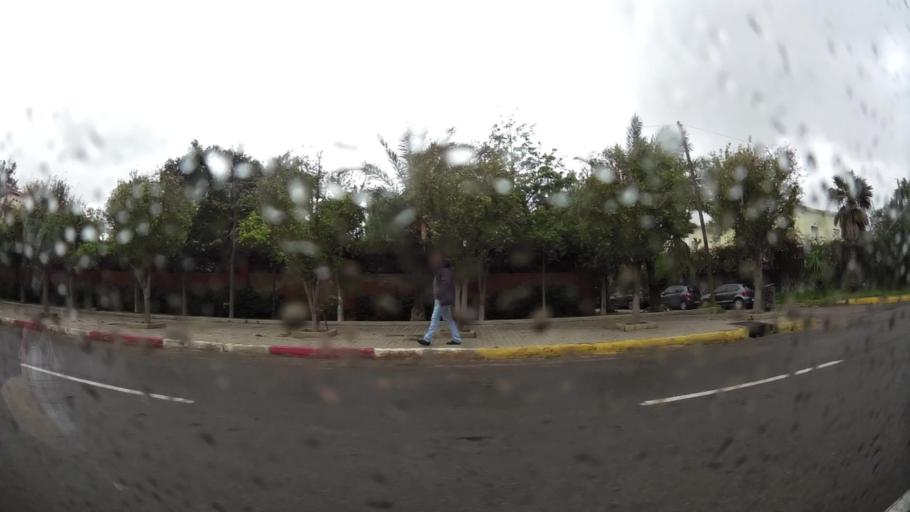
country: MA
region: Grand Casablanca
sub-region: Casablanca
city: Casablanca
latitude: 33.5309
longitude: -7.6204
